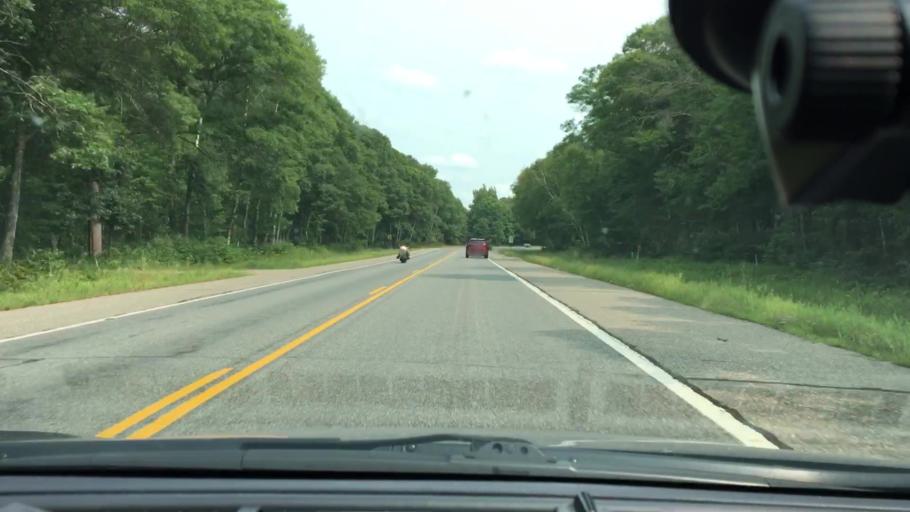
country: US
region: Minnesota
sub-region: Crow Wing County
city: Breezy Point
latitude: 46.5298
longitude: -94.1877
